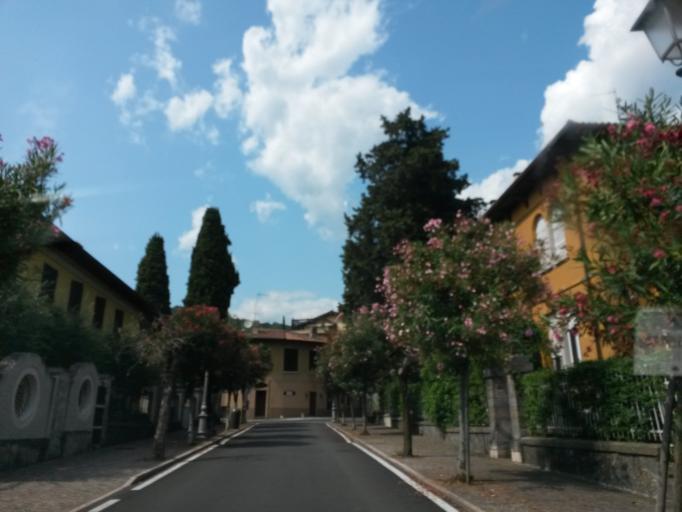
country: IT
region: Lombardy
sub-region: Provincia di Brescia
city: Gardone Riviera
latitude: 45.6143
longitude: 10.5527
